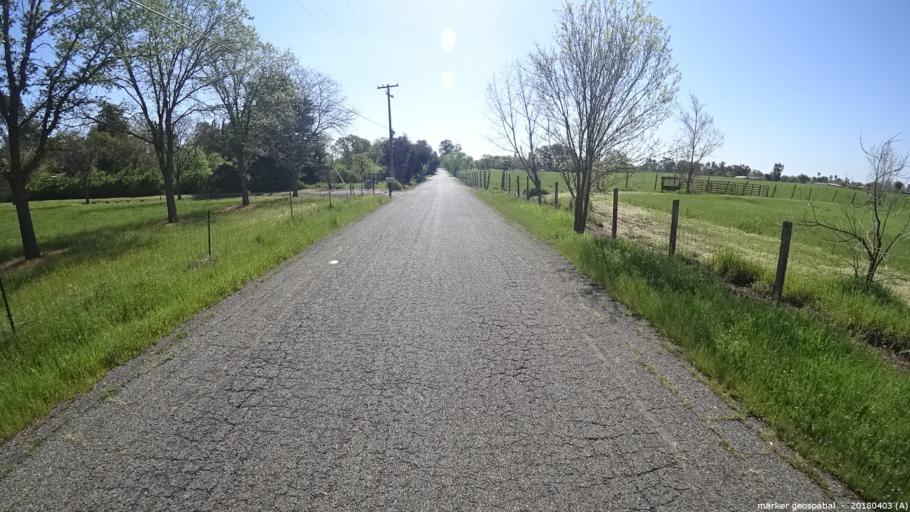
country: US
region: California
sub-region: Sacramento County
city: Wilton
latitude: 38.4308
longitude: -121.2163
